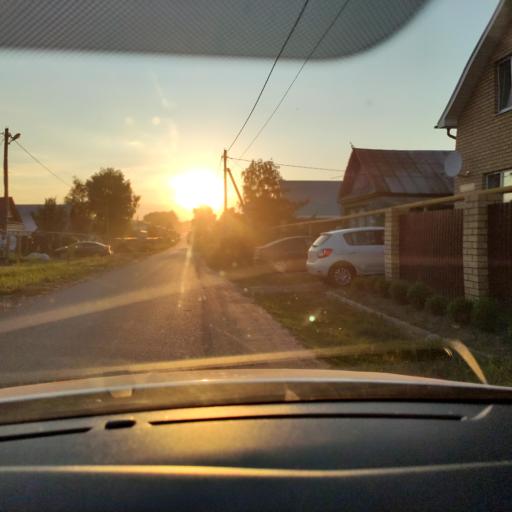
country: RU
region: Tatarstan
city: Stolbishchi
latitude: 55.7474
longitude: 49.3046
